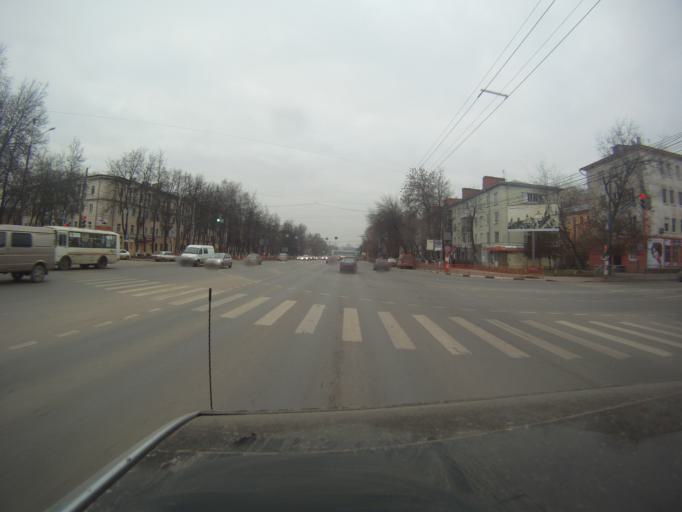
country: RU
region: Nizjnij Novgorod
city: Nizhniy Novgorod
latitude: 56.3039
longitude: 43.9844
